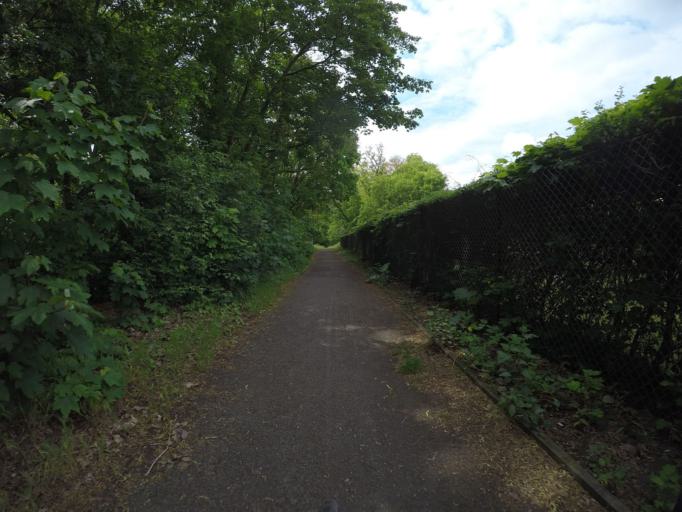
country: DE
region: Berlin
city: Reinickendorf
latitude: 52.5513
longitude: 13.3117
